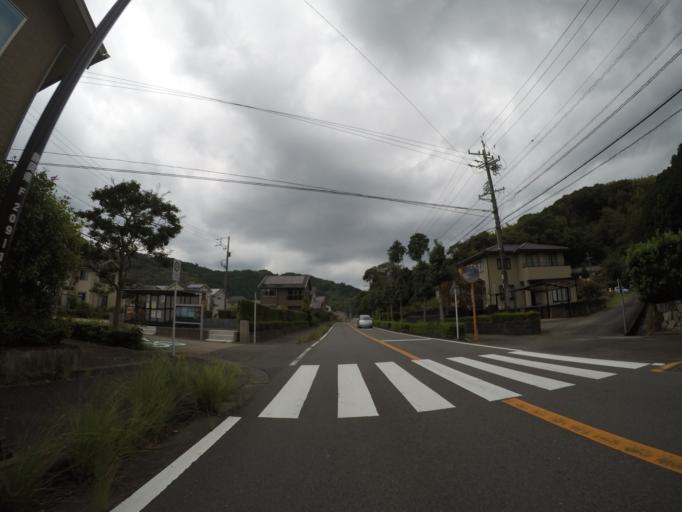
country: JP
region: Shizuoka
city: Fujieda
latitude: 34.8989
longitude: 138.2630
